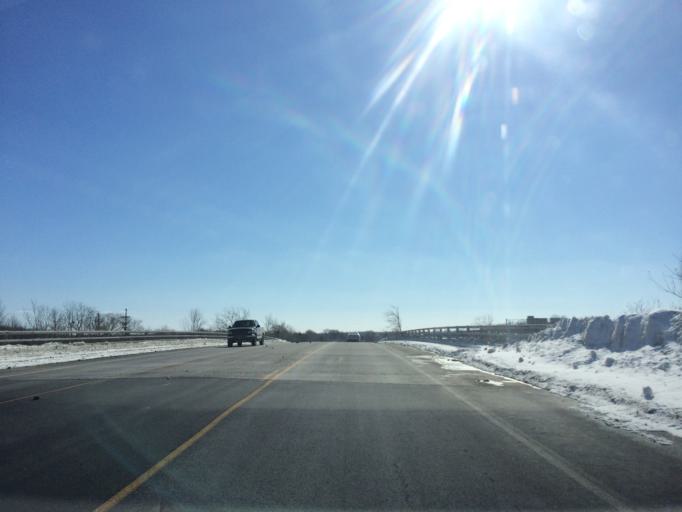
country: US
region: New York
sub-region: Monroe County
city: Rochester
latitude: 43.1059
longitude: -77.5989
